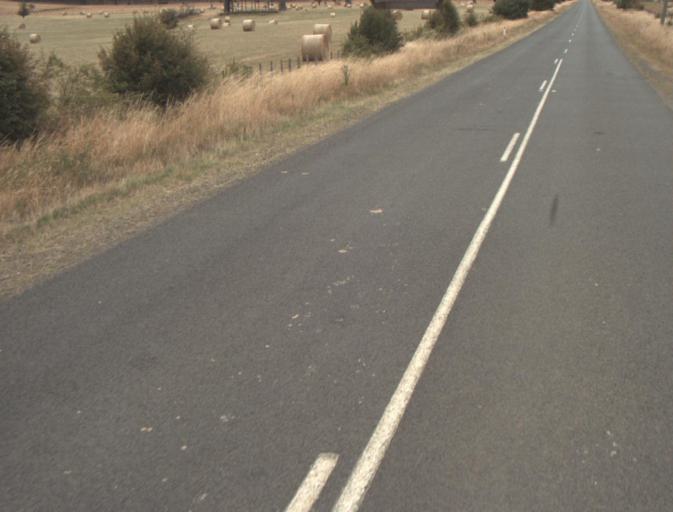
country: AU
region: Tasmania
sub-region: Northern Midlands
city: Evandale
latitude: -41.5040
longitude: 147.4838
